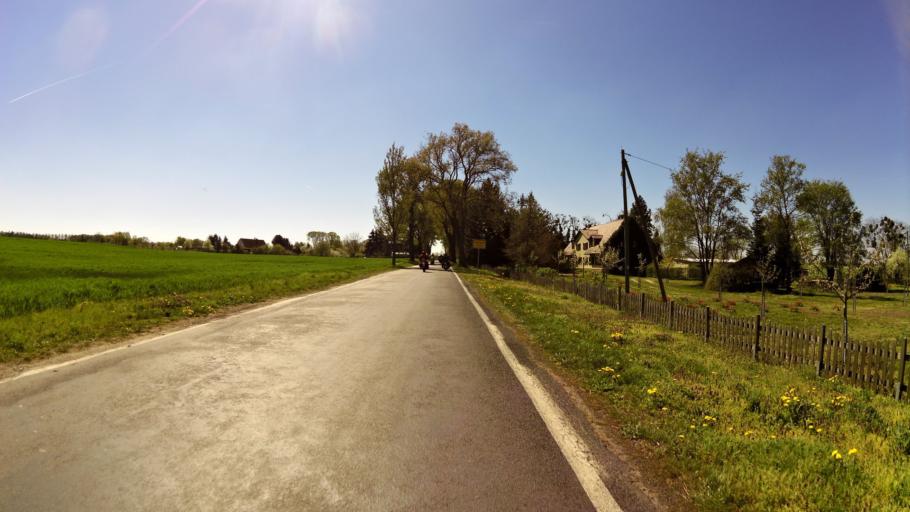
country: DE
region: Brandenburg
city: Werftpfuhl
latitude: 52.6436
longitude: 13.7926
